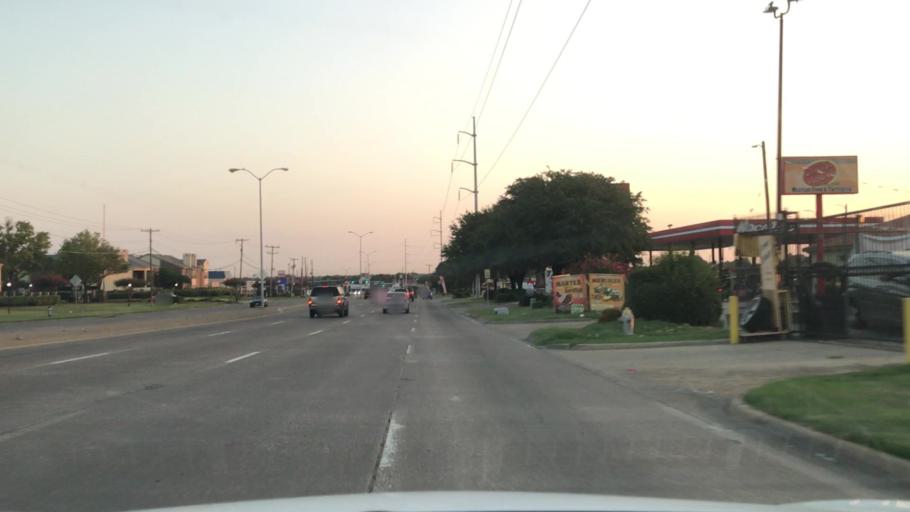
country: US
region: Texas
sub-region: Dallas County
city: Mesquite
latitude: 32.8032
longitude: -96.6823
